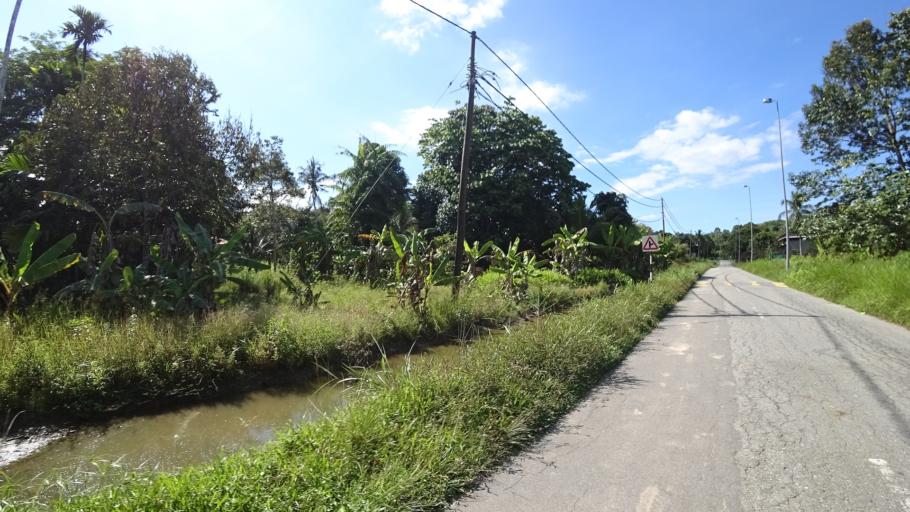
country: BN
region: Tutong
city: Tutong
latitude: 4.7410
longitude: 114.7894
